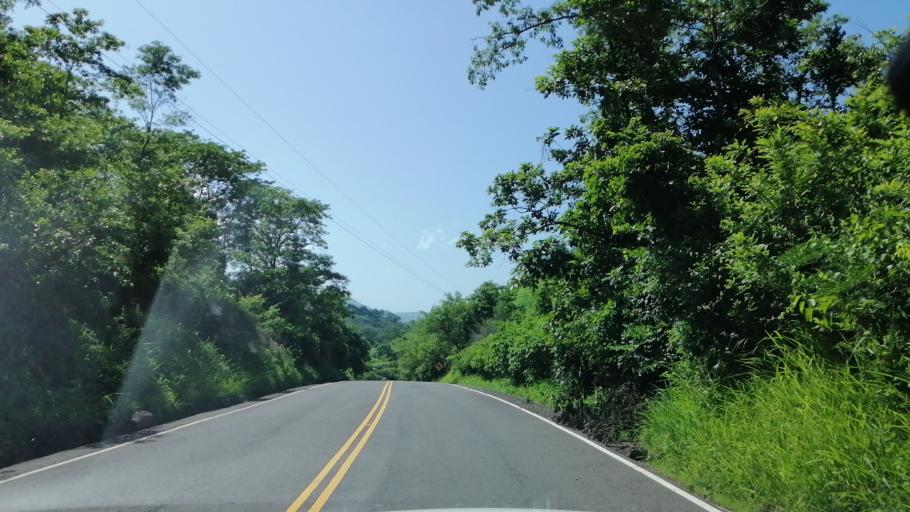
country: HN
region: Lempira
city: La Virtud
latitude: 13.9554
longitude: -88.7498
